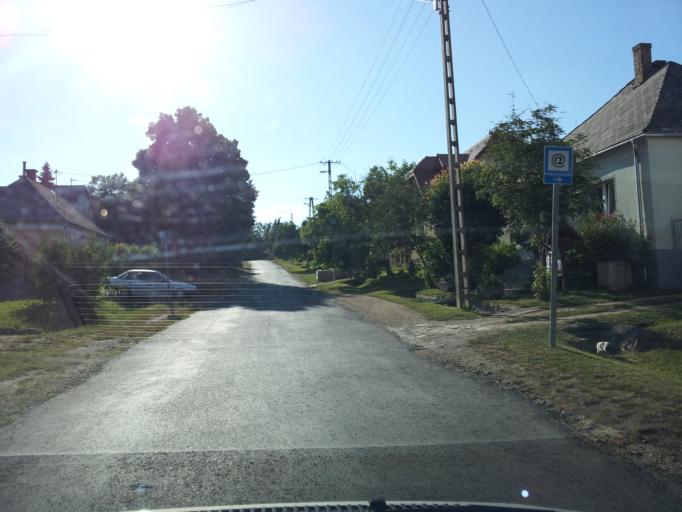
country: HU
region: Veszprem
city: Zirc
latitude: 47.2069
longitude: 17.8632
